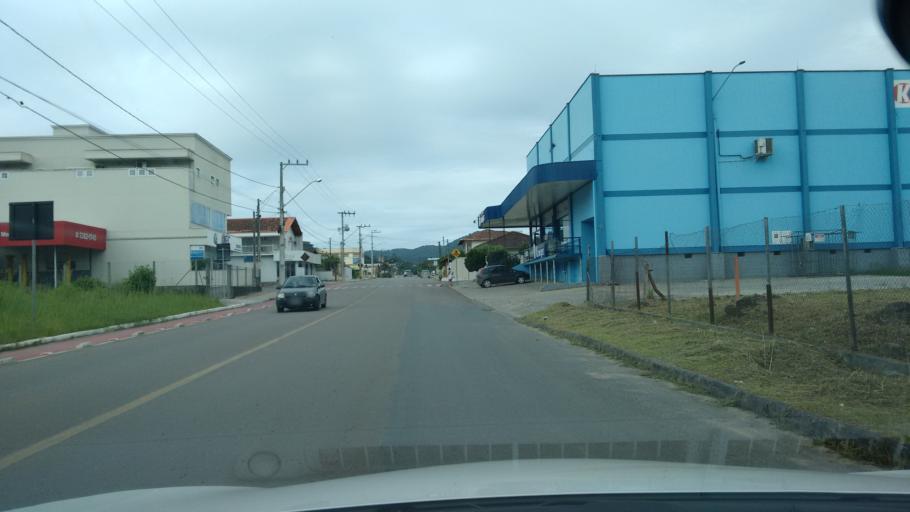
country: BR
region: Santa Catarina
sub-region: Timbo
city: Timbo
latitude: -26.8126
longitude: -49.2722
